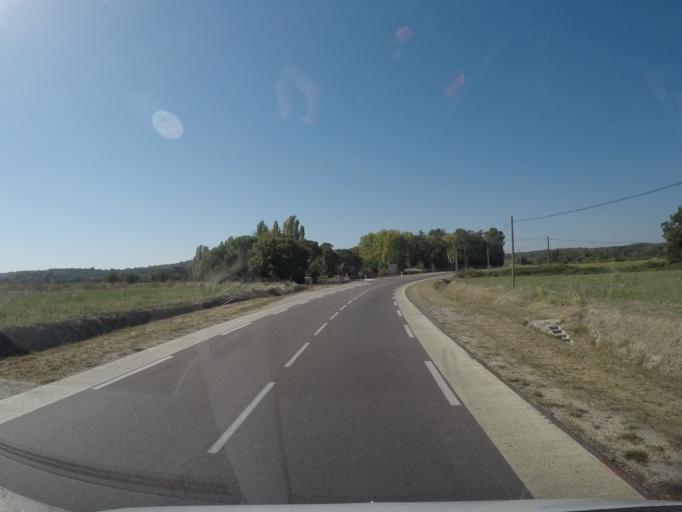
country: FR
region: Languedoc-Roussillon
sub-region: Departement du Gard
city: Uzes
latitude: 44.0007
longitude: 4.3998
